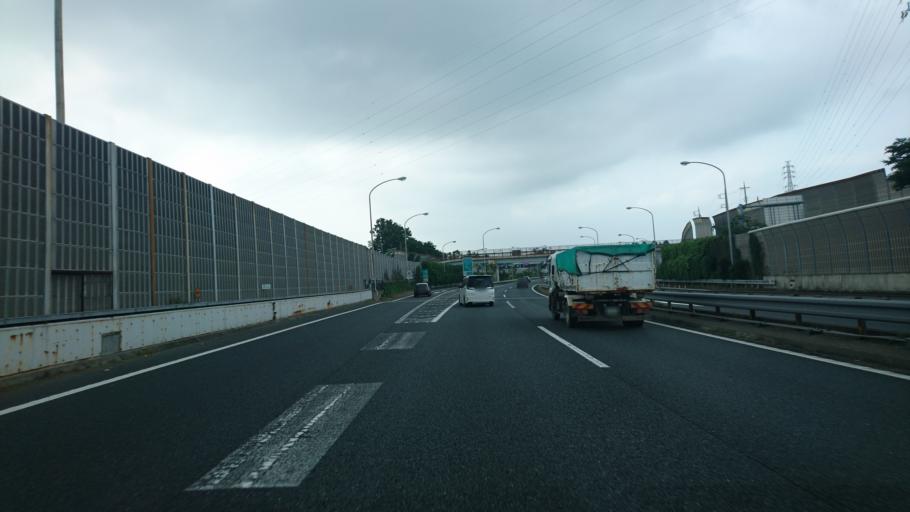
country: JP
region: Chiba
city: Chiba
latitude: 35.5874
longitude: 140.1464
